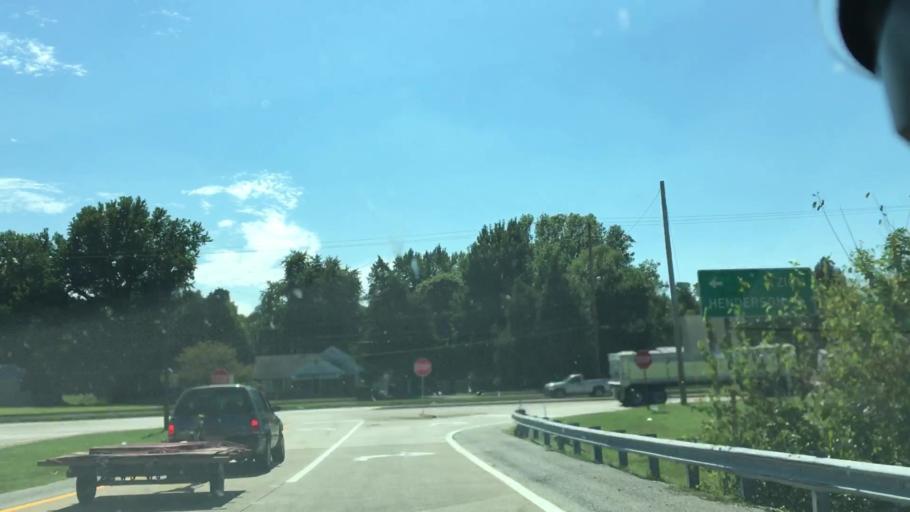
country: US
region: Kentucky
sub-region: Henderson County
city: Henderson
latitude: 37.8309
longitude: -87.5650
